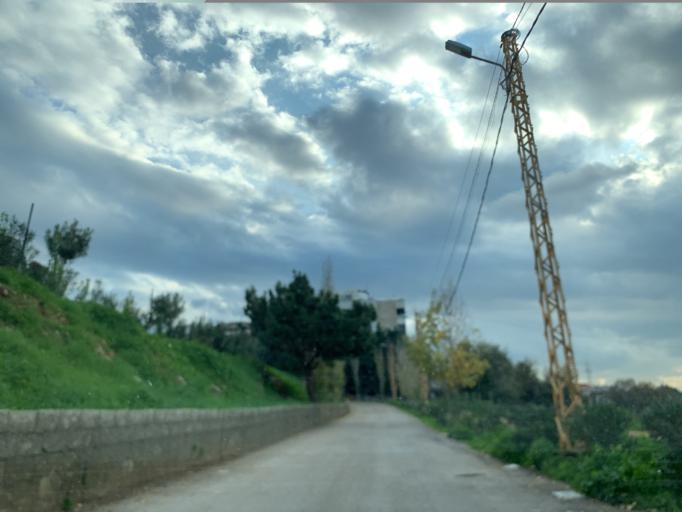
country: LB
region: Mont-Liban
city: Baabda
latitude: 33.8510
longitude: 35.5663
